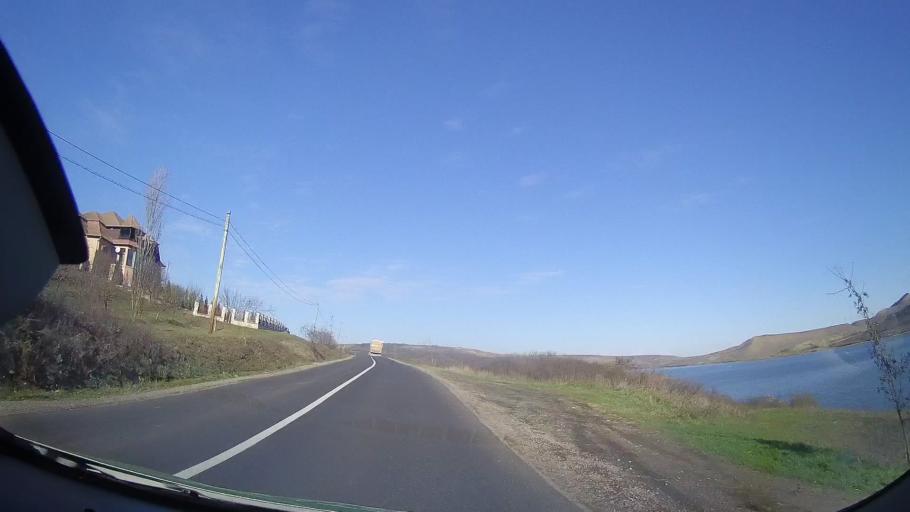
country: RO
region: Mures
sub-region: Comuna Zau De Campie
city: Zau de Campie
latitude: 46.6262
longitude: 24.1330
